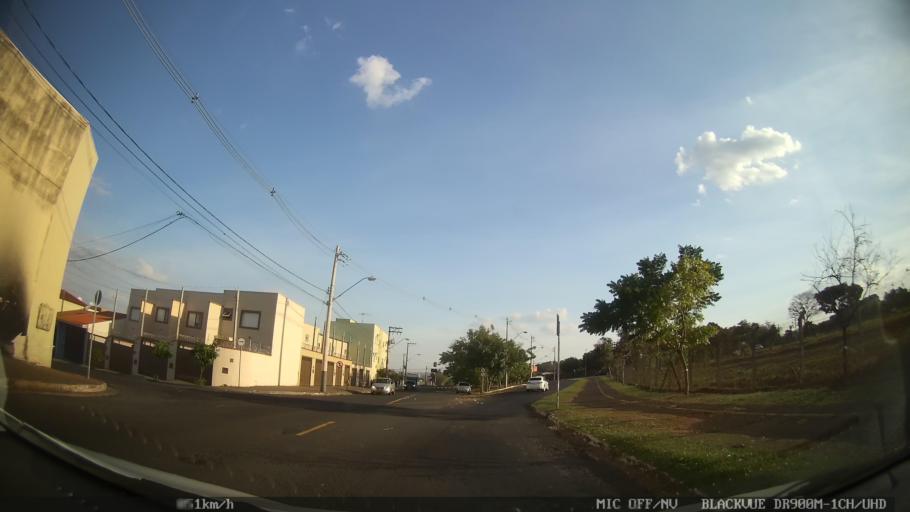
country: BR
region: Sao Paulo
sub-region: Ribeirao Preto
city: Ribeirao Preto
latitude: -21.1635
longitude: -47.8435
